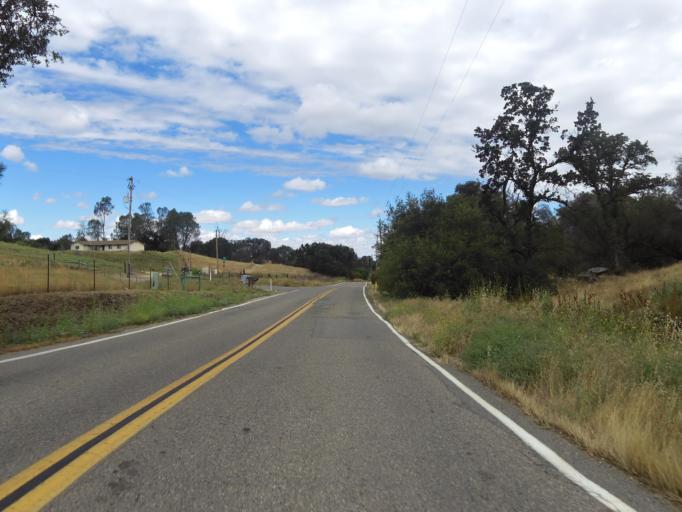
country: US
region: California
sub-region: Madera County
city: Yosemite Lakes
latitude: 37.2423
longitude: -119.8405
